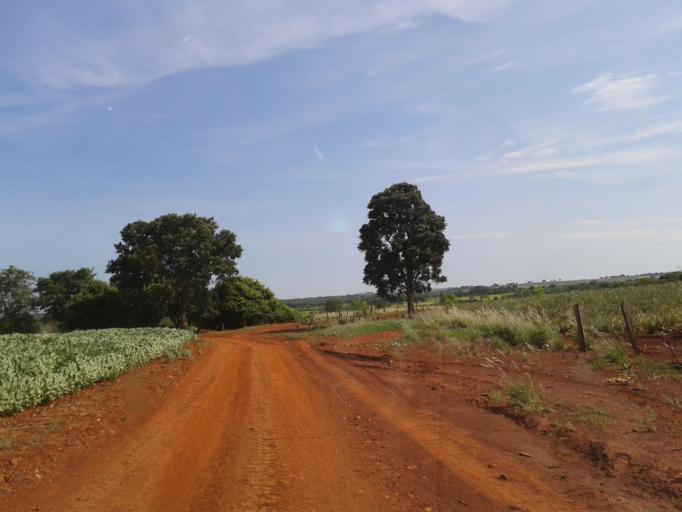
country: BR
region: Minas Gerais
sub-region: Centralina
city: Centralina
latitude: -18.7056
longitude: -49.2046
